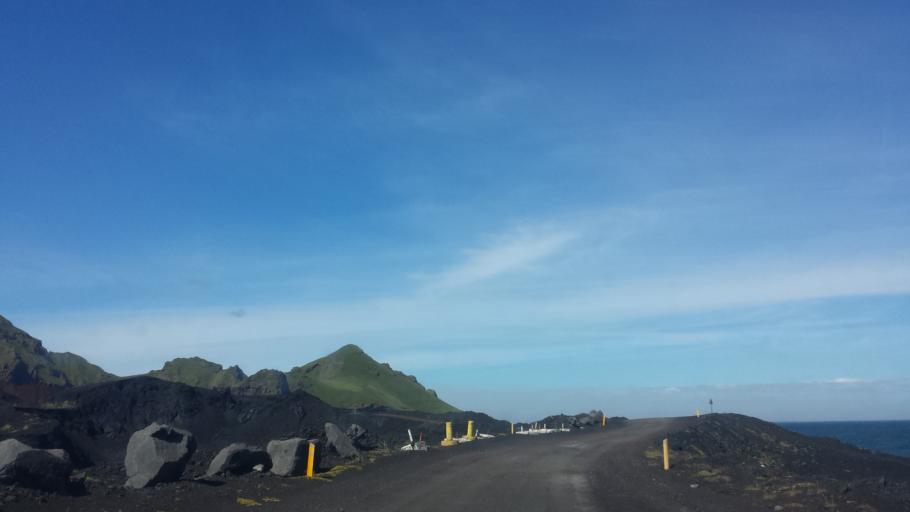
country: IS
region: South
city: Vestmannaeyjar
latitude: 63.4373
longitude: -20.2299
